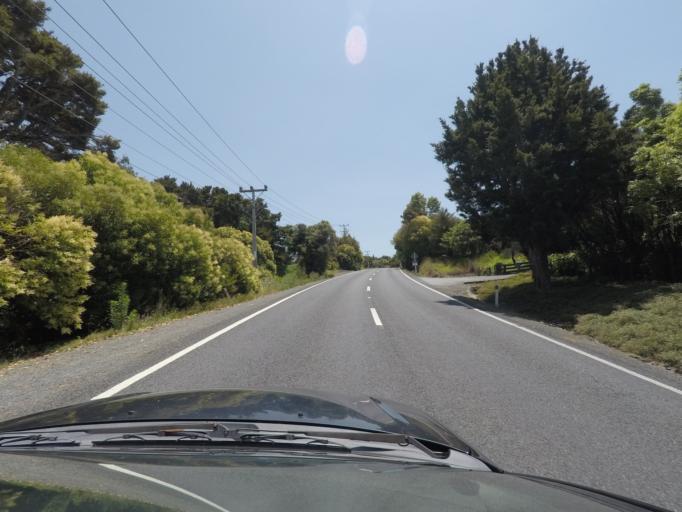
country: NZ
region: Auckland
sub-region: Auckland
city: Warkworth
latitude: -36.3911
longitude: 174.6607
